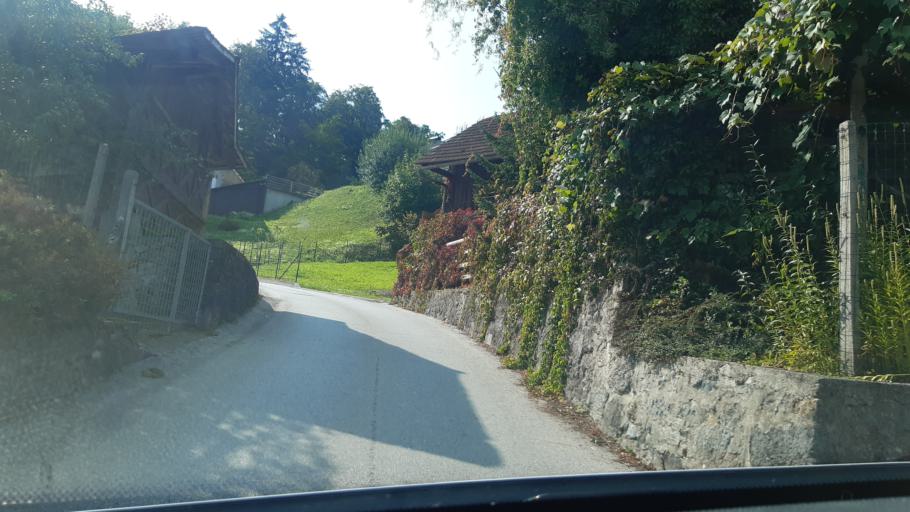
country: SI
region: Lukovica
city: Lukovica pri Domzalah
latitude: 46.1691
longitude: 14.6898
